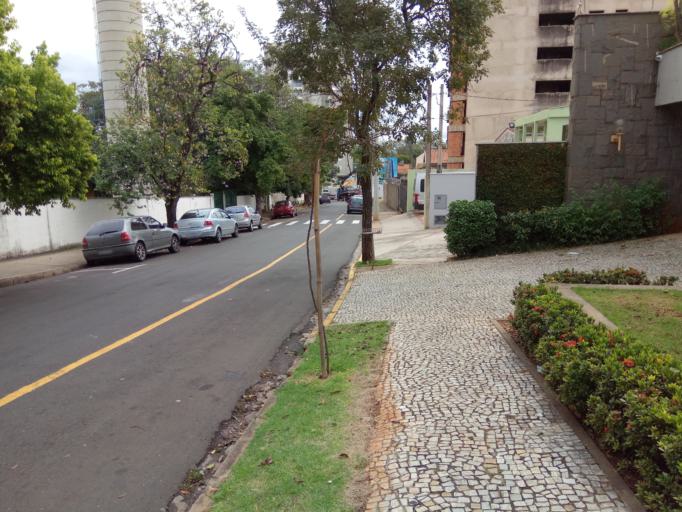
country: BR
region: Sao Paulo
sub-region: Piracicaba
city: Piracicaba
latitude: -22.7140
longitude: -47.6453
